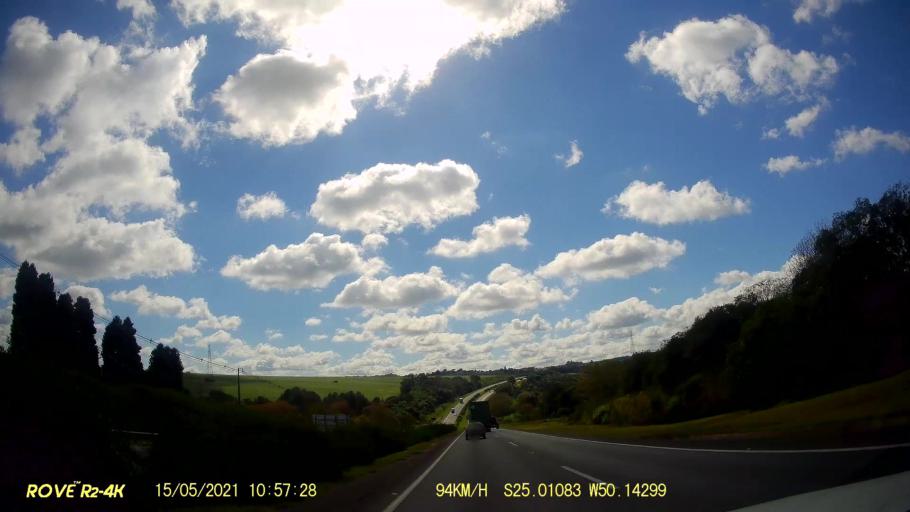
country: BR
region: Parana
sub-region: Carambei
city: Carambei
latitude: -25.0110
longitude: -50.1431
